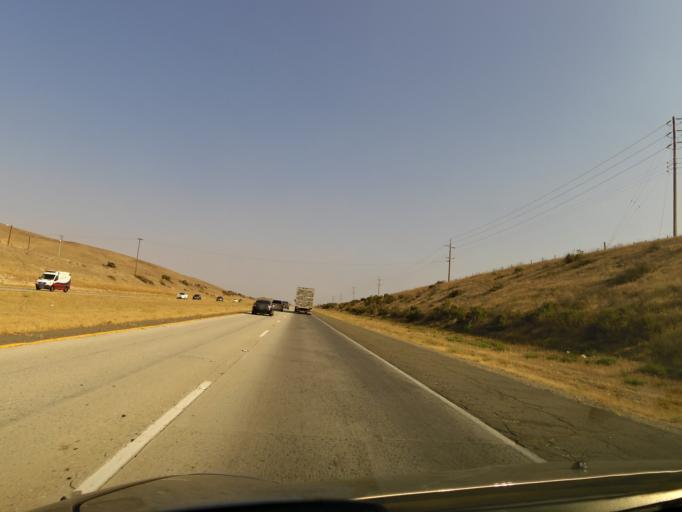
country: US
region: California
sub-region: Monterey County
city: King City
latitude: 36.1674
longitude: -121.0569
